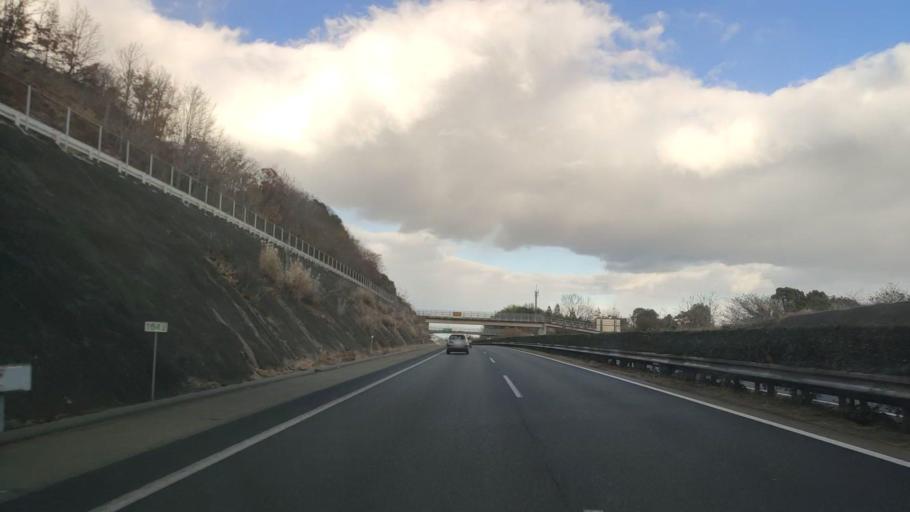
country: JP
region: Okayama
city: Kamogatacho-kamogata
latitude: 34.5716
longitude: 133.6671
